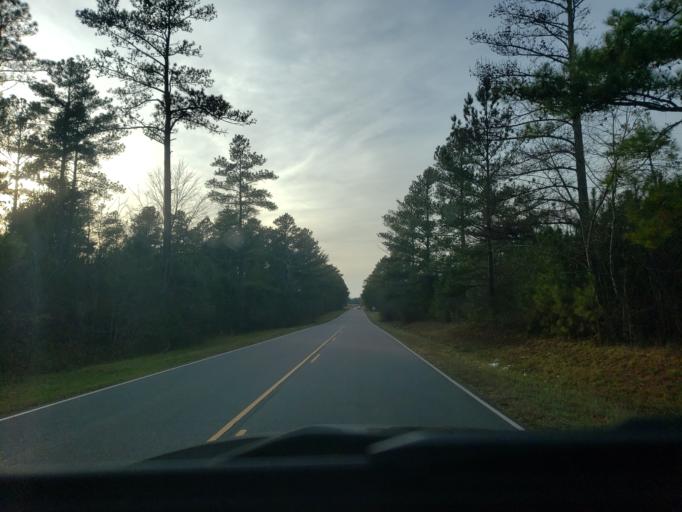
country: US
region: North Carolina
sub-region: Cleveland County
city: Boiling Springs
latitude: 35.3048
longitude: -81.7107
